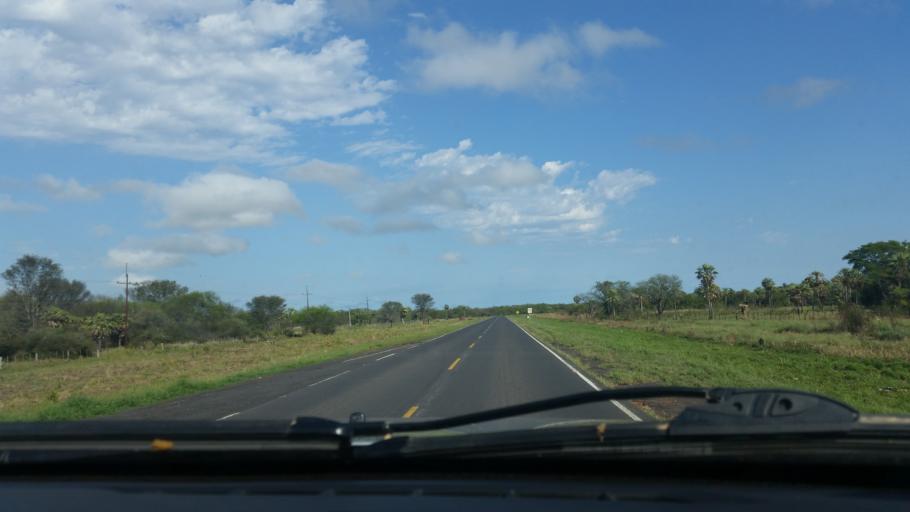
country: PY
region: Presidente Hayes
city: Benjamin Aceval
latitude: -24.9088
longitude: -57.6400
